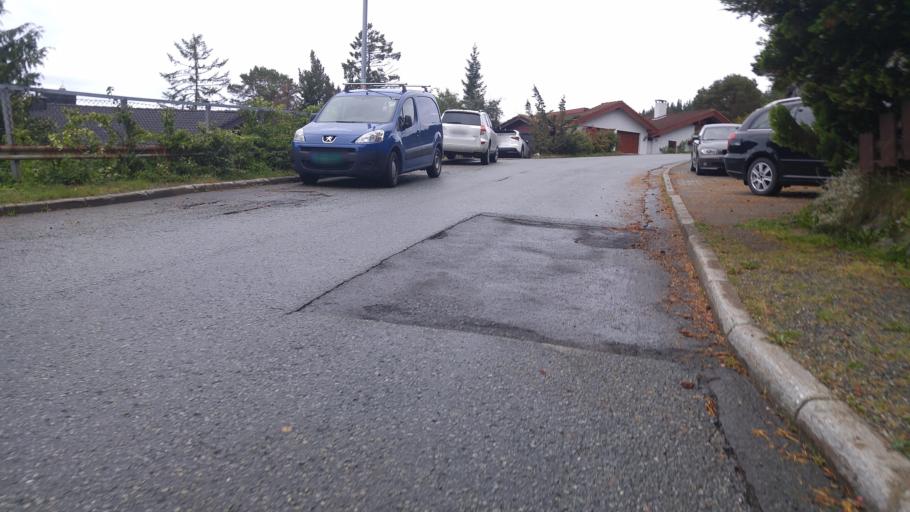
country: NO
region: Sor-Trondelag
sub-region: Trondheim
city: Trondheim
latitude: 63.4519
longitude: 10.3027
